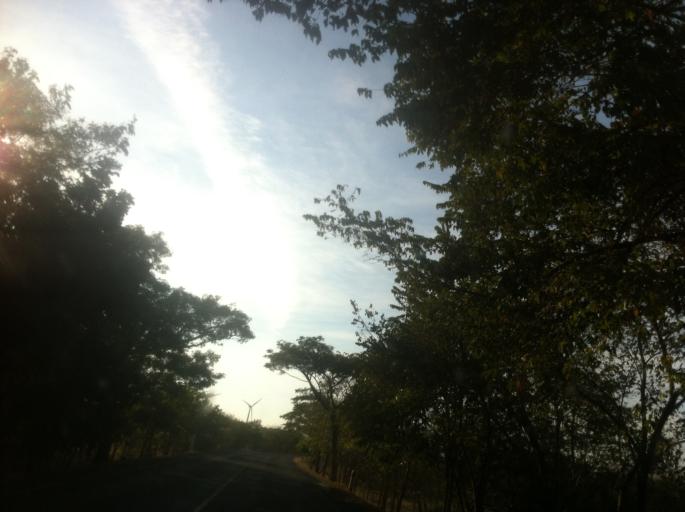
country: NI
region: Rivas
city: San Jorge
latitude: 11.3081
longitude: -85.6928
